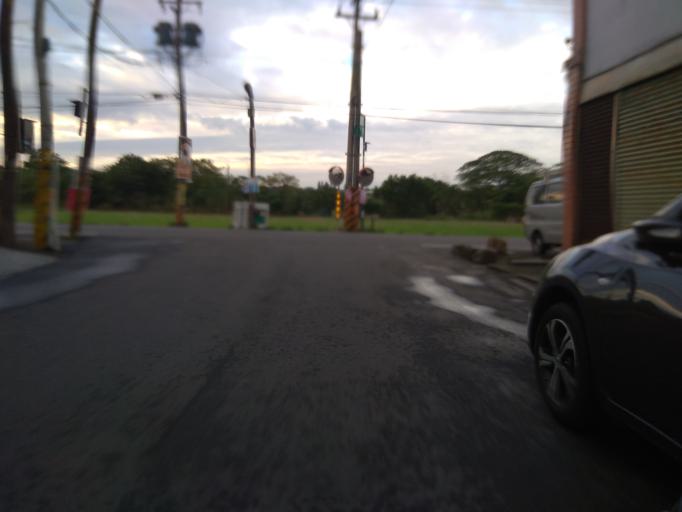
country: TW
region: Taiwan
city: Taoyuan City
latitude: 24.9493
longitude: 121.1920
